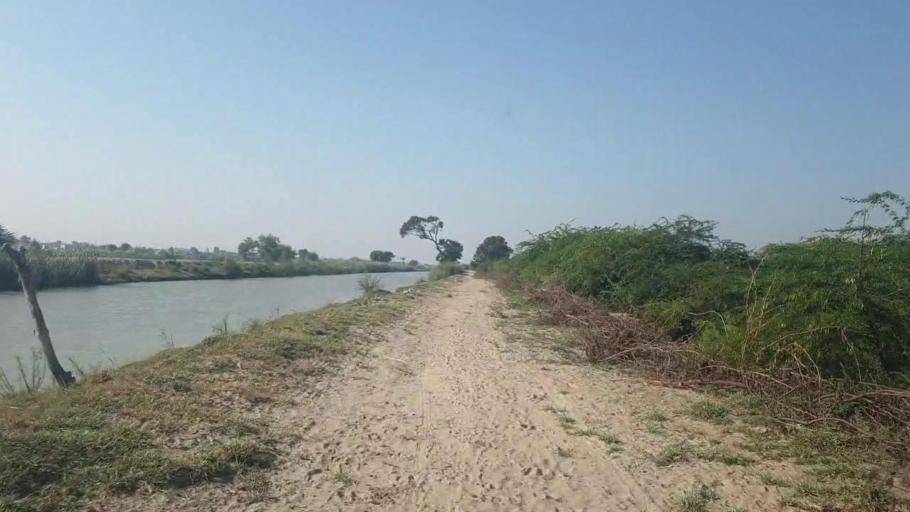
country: PK
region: Sindh
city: Badin
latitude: 24.6992
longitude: 68.8778
